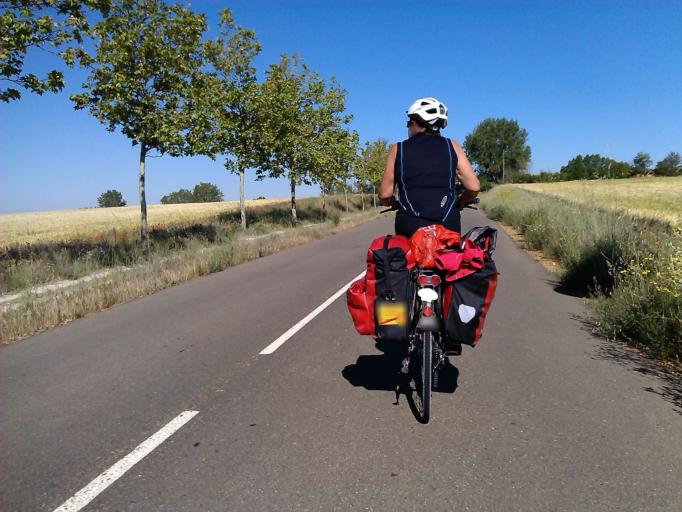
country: ES
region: Castille and Leon
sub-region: Provincia de Leon
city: Bercianos del Real Camino
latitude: 42.3887
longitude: -5.1288
